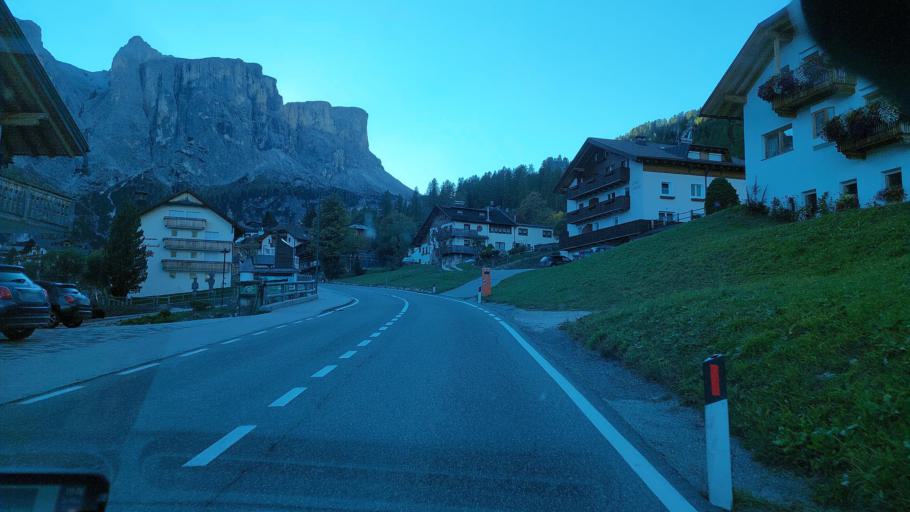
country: IT
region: Trentino-Alto Adige
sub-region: Bolzano
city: Corvara in Badia
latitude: 46.5530
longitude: 11.8484
